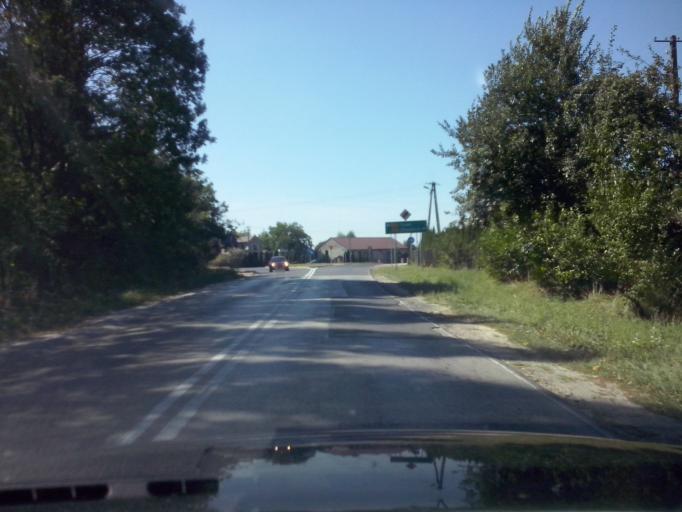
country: PL
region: Swietokrzyskie
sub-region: Powiat staszowski
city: Szydlow
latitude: 50.5918
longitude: 21.0080
